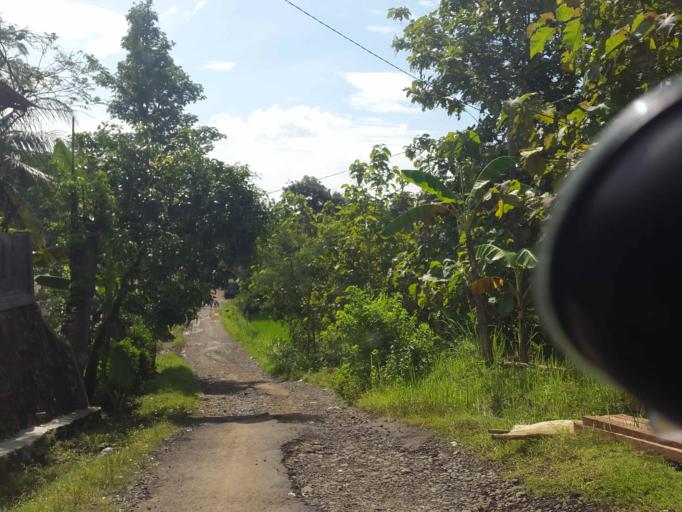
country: ID
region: Central Java
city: Garbi
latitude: -7.4572
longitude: 109.1887
